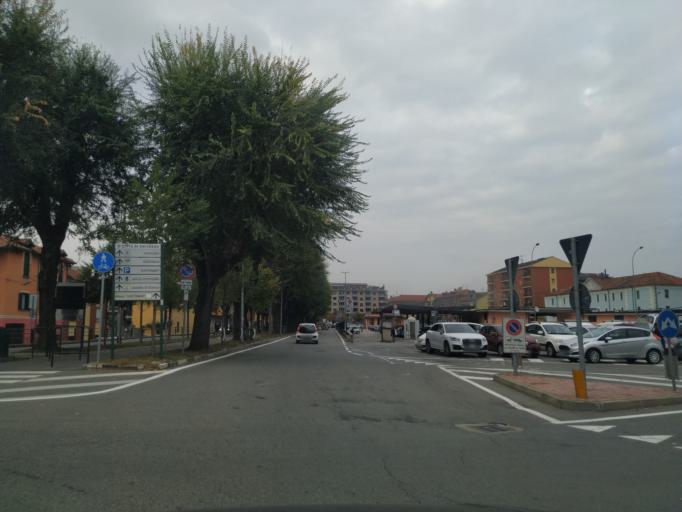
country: IT
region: Piedmont
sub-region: Provincia di Torino
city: Chivasso
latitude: 45.1873
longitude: 7.8859
